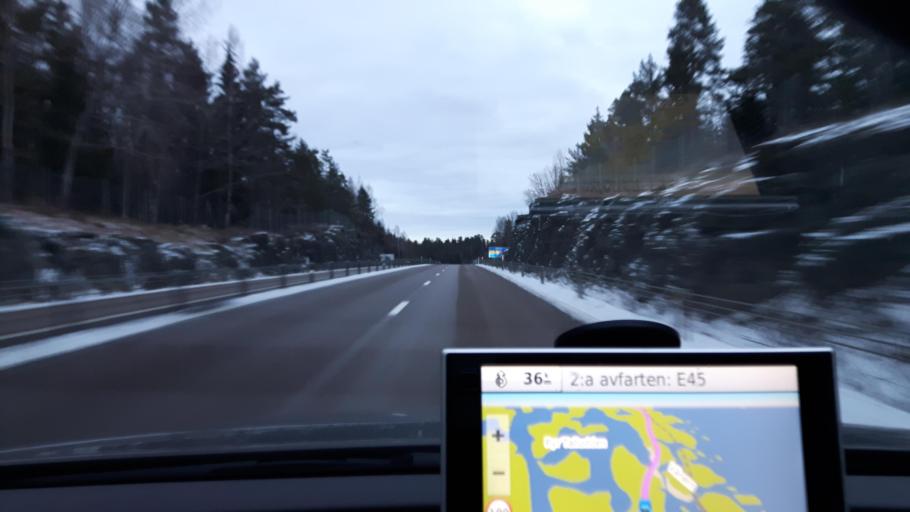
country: SE
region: Vaestra Goetaland
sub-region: Melleruds Kommun
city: Mellerud
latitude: 58.7705
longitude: 12.4935
